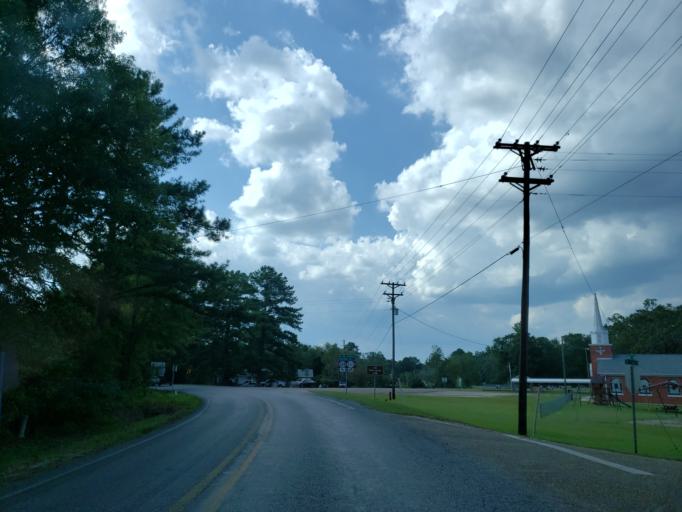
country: US
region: Mississippi
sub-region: Jones County
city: Sharon
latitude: 31.9186
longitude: -89.0197
